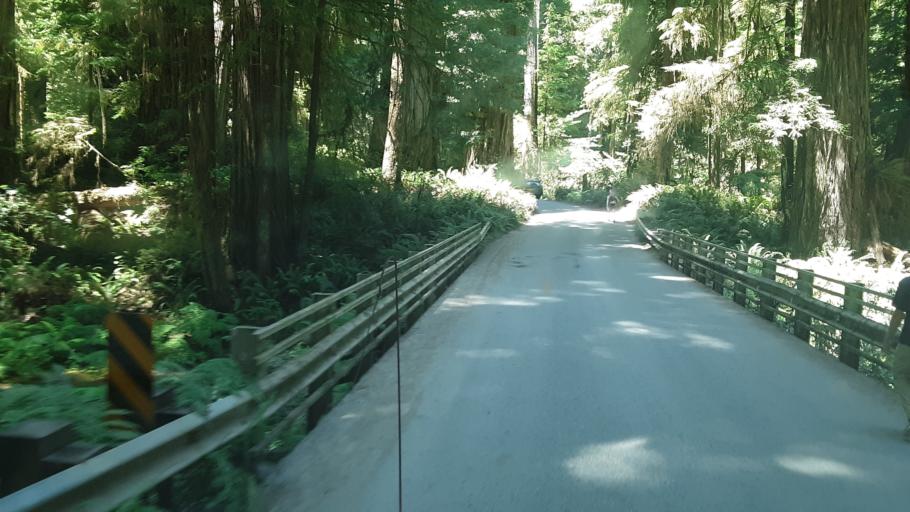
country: US
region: California
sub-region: Del Norte County
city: Bertsch-Oceanview
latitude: 41.8125
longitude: -124.1092
